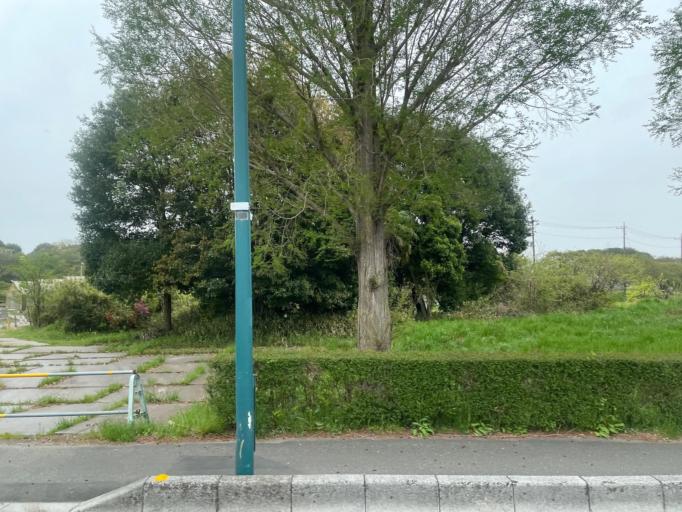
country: JP
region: Saitama
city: Saitama
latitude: 35.8933
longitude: 139.7029
